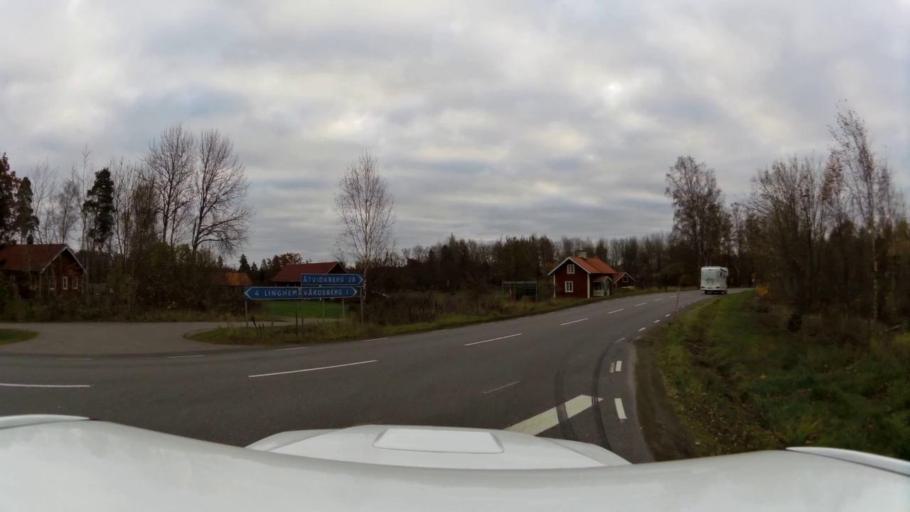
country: SE
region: OEstergoetland
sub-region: Linkopings Kommun
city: Linghem
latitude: 58.4097
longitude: 15.7632
